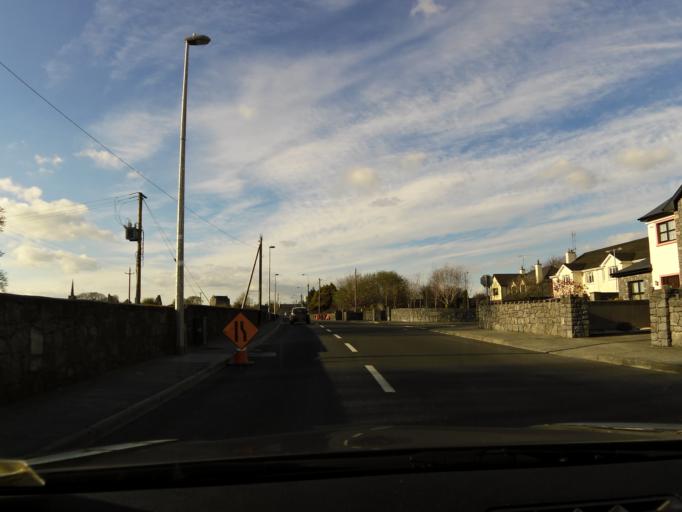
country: IE
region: Connaught
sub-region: County Galway
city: Athenry
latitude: 53.2959
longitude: -8.7428
